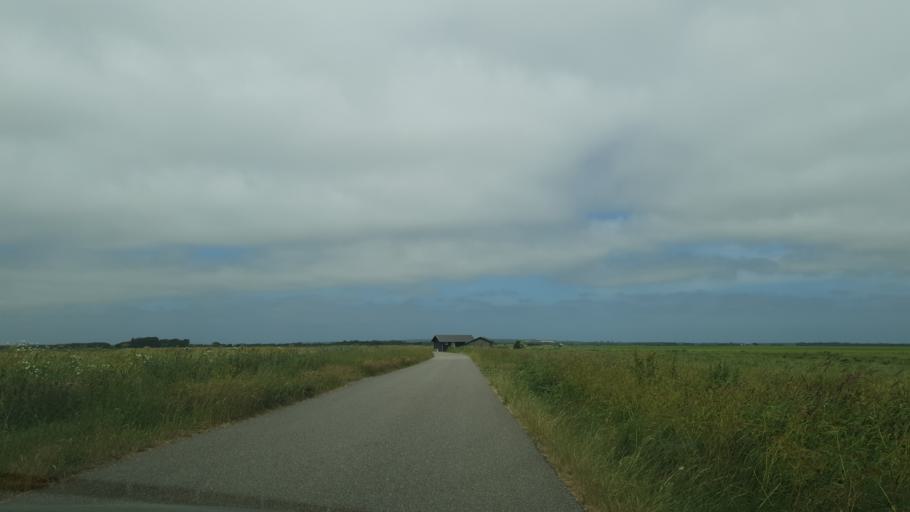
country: DK
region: Central Jutland
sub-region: Ringkobing-Skjern Kommune
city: Skjern
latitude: 55.9242
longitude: 8.4023
